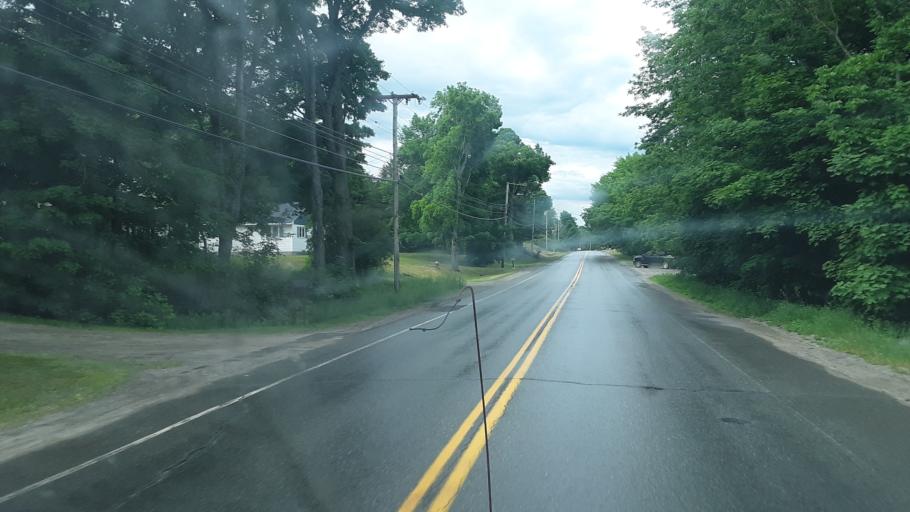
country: US
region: Maine
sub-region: Penobscot County
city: Lincoln
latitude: 45.3815
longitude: -68.4991
